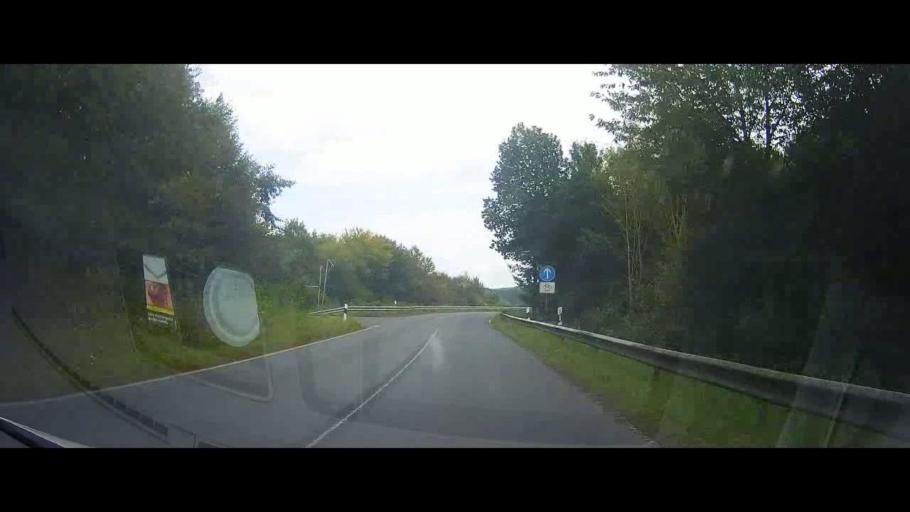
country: DE
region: Lower Saxony
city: Adelebsen
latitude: 51.5736
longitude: 9.7479
